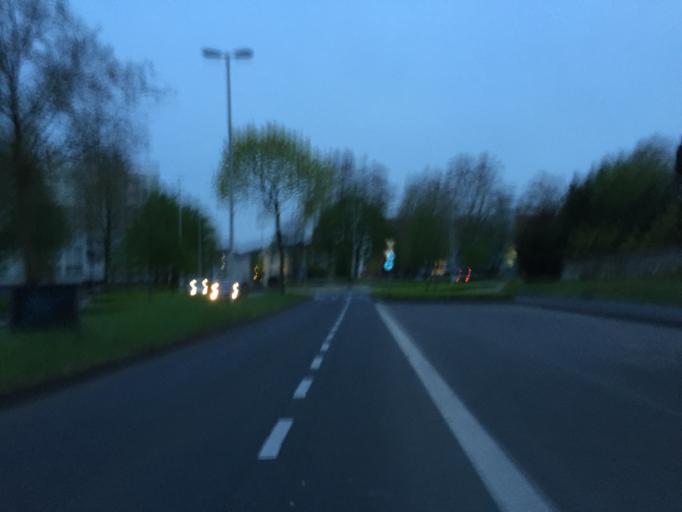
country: DE
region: North Rhine-Westphalia
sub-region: Regierungsbezirk Koln
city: Alfter
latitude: 50.7406
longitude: 7.0471
